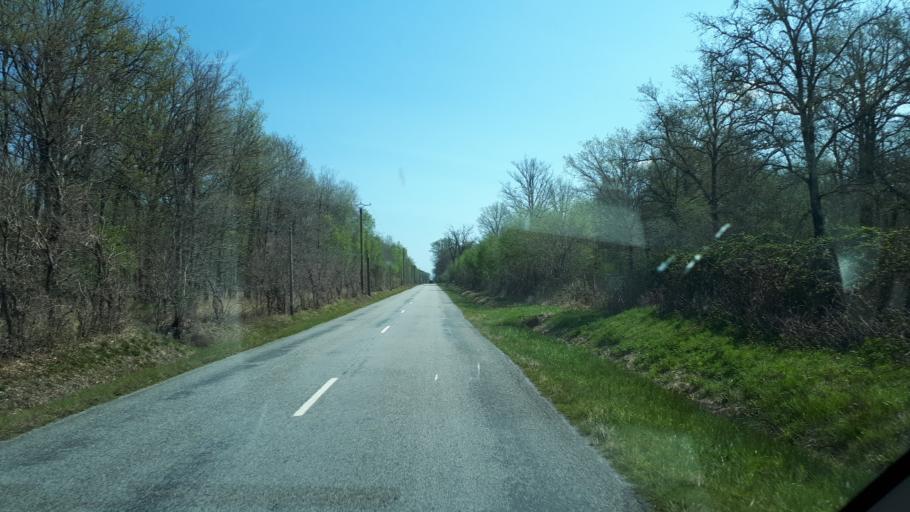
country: FR
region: Centre
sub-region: Departement du Loir-et-Cher
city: Theillay
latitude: 47.3142
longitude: 2.0993
